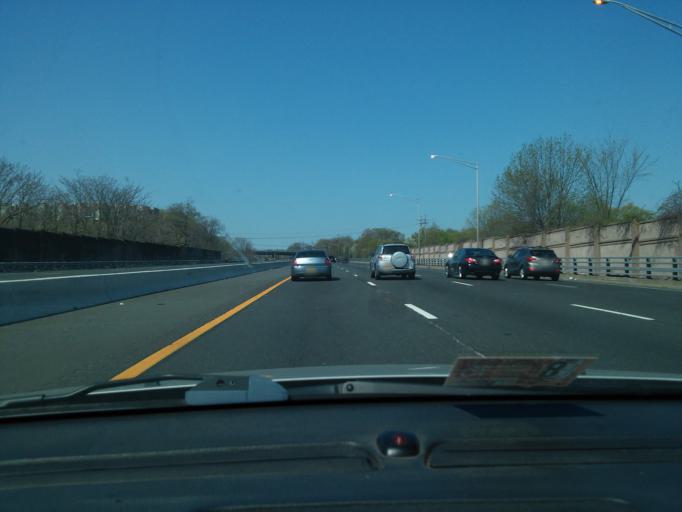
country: US
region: New Jersey
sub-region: Union County
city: Springfield
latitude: 40.7118
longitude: -74.3245
